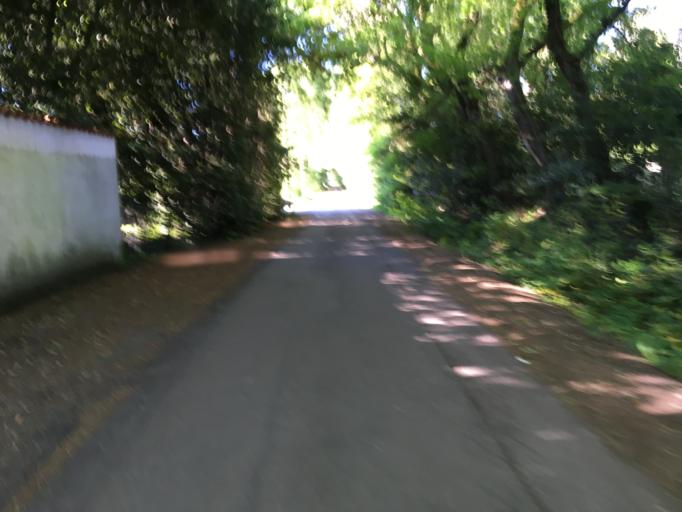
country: FR
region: Poitou-Charentes
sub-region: Departement de la Charente-Maritime
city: Lagord
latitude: 46.1811
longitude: -1.1728
